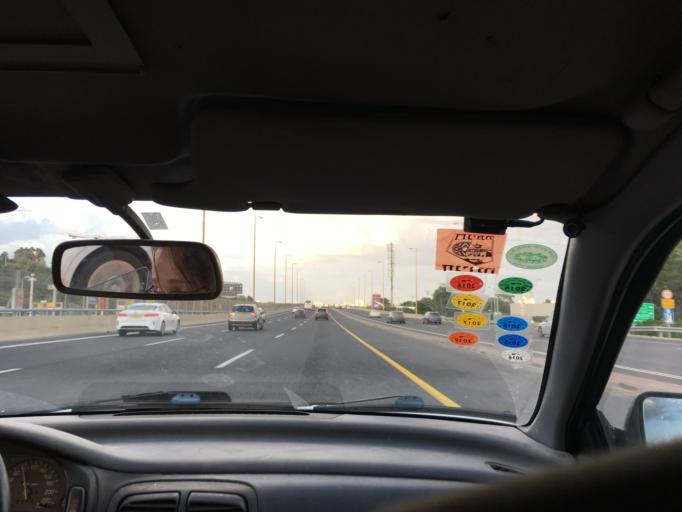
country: IL
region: Tel Aviv
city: Ramat Gan
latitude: 32.1030
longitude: 34.8045
